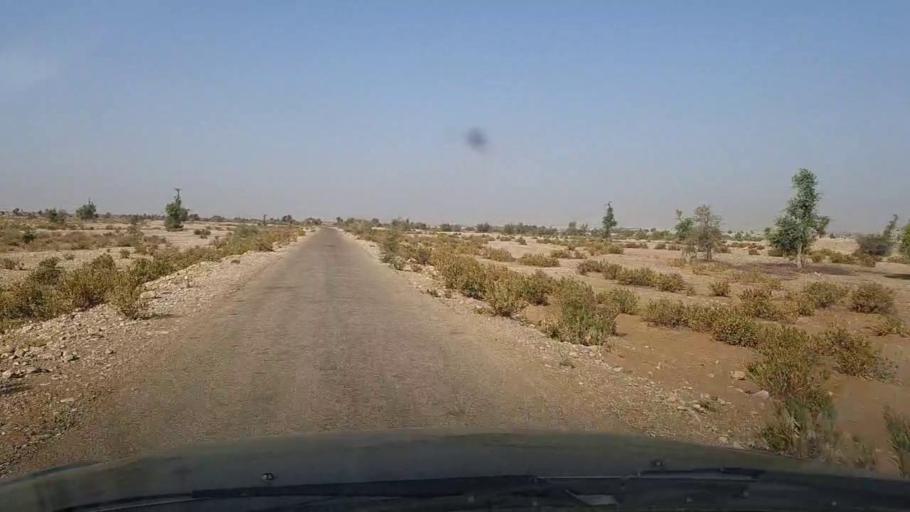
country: PK
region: Sindh
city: Sann
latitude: 25.9409
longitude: 68.0320
